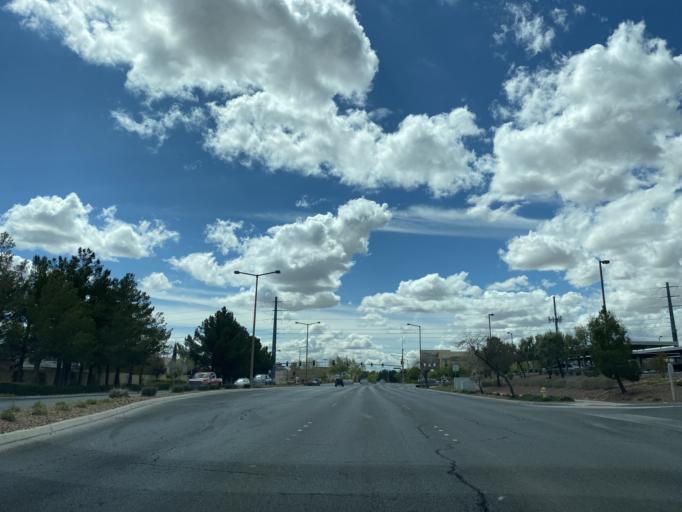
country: US
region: Nevada
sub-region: Clark County
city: Summerlin South
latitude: 36.1606
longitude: -115.3143
